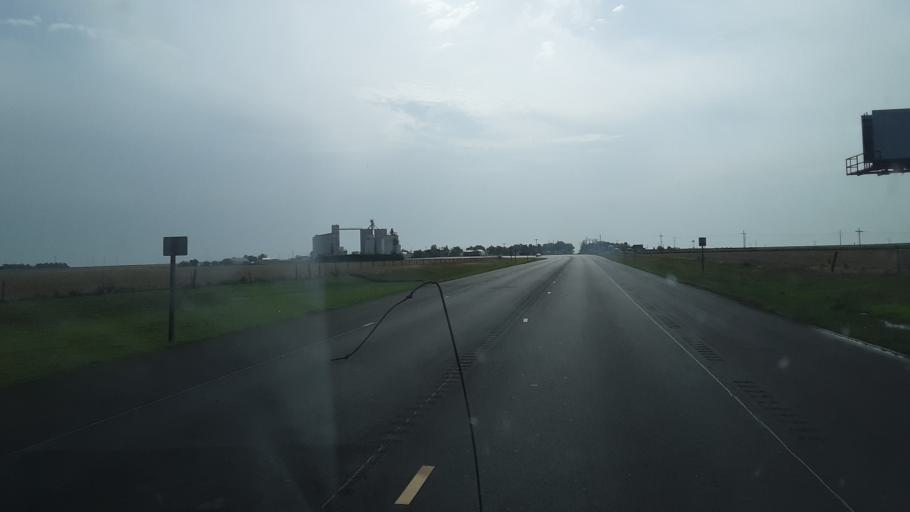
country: US
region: Kansas
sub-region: Ford County
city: Dodge City
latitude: 37.7789
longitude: -99.9044
